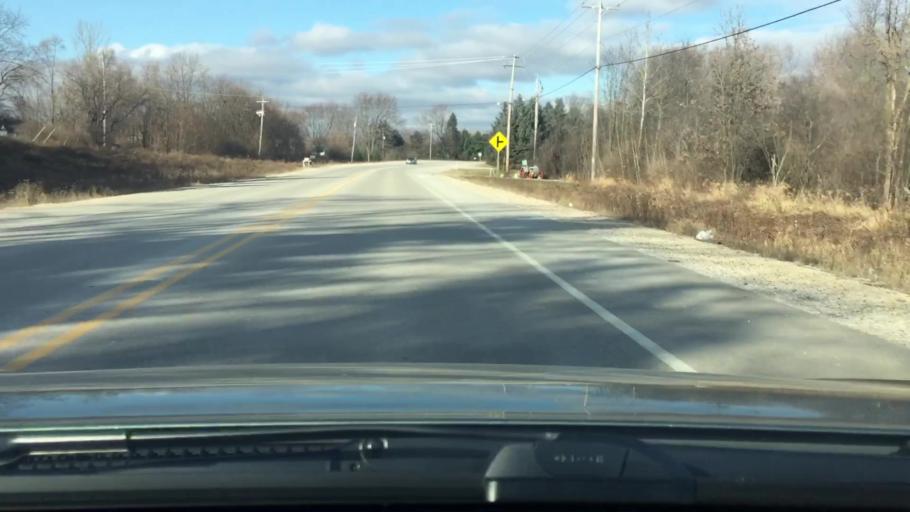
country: US
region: Wisconsin
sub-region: Waukesha County
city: Wales
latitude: 42.9820
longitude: -88.3790
